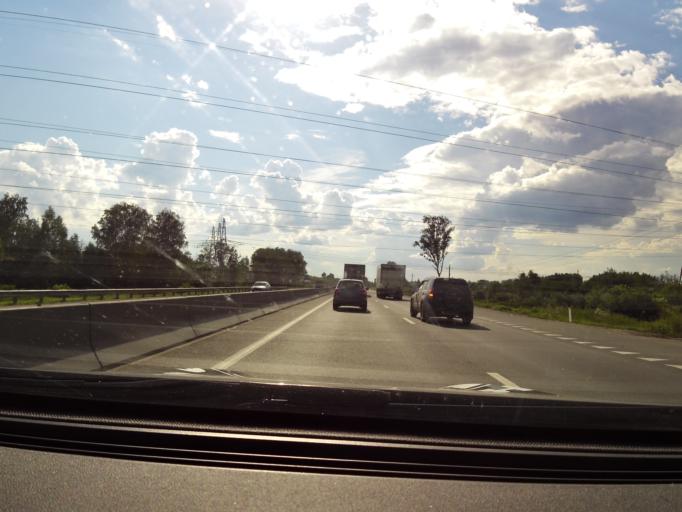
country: RU
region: Nizjnij Novgorod
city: Babino
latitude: 56.3061
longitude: 43.6659
